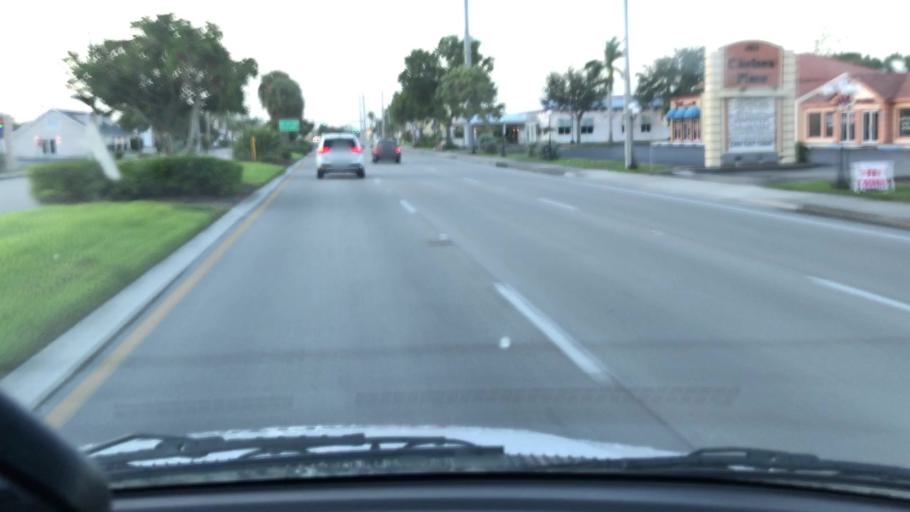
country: US
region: Florida
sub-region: Lee County
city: Cape Coral
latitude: 26.5873
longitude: -81.9420
